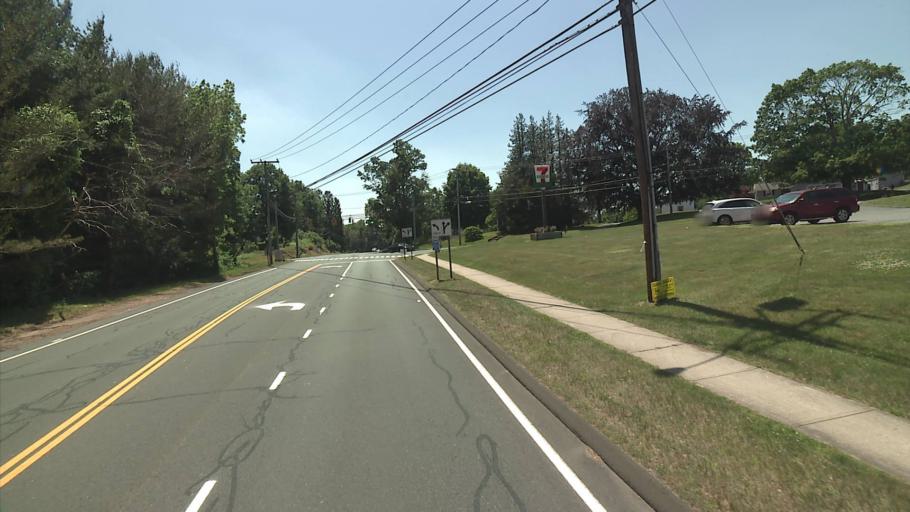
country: US
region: Connecticut
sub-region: Tolland County
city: Rockville
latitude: 41.8461
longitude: -72.4541
